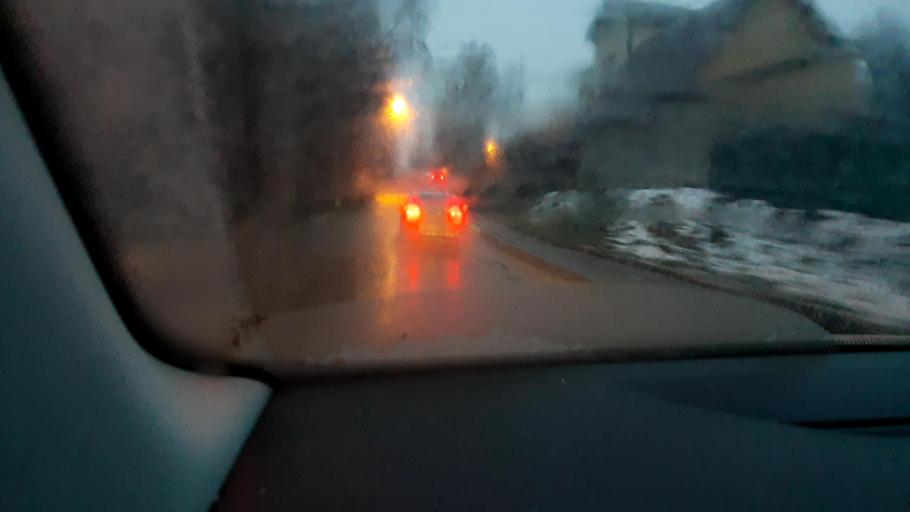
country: RU
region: Moscow
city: Annino
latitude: 55.5695
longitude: 37.6156
